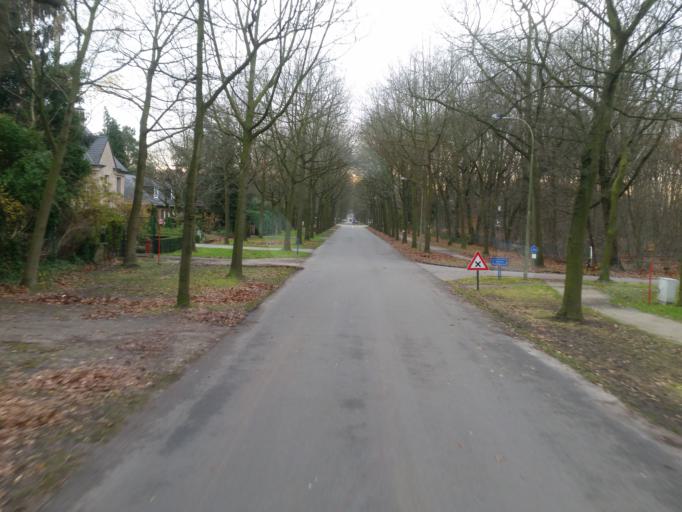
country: BE
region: Flanders
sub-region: Provincie Antwerpen
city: Brasschaat
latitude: 51.3156
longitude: 4.4987
